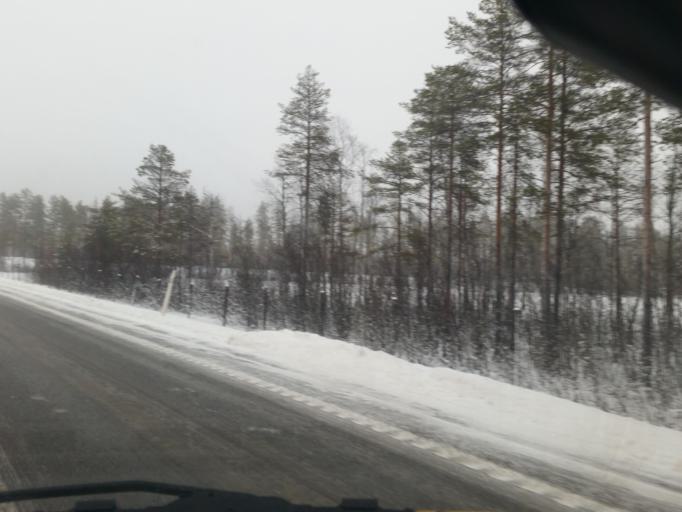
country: SE
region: Norrbotten
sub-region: Pitea Kommun
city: Hortlax
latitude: 65.0890
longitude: 21.4816
